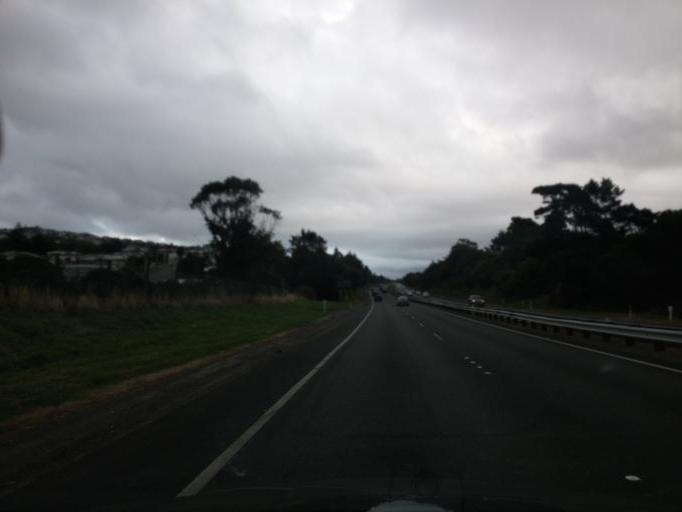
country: NZ
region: Wellington
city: Petone
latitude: -41.2095
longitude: 174.8163
